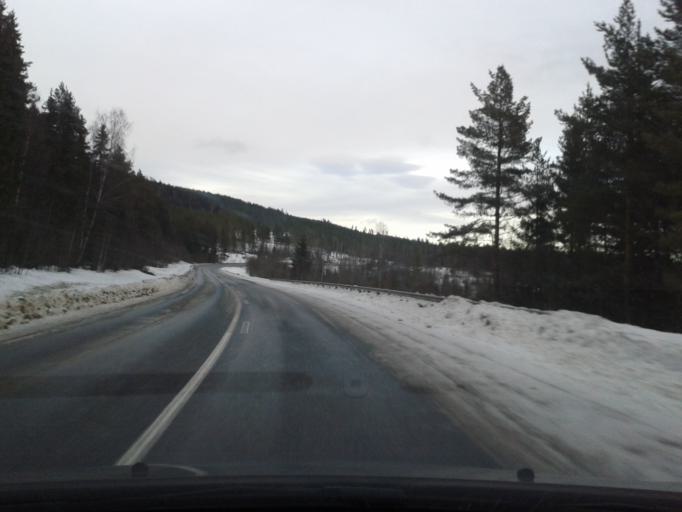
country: SE
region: Vaesternorrland
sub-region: Solleftea Kommun
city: Solleftea
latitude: 63.3328
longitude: 17.1266
